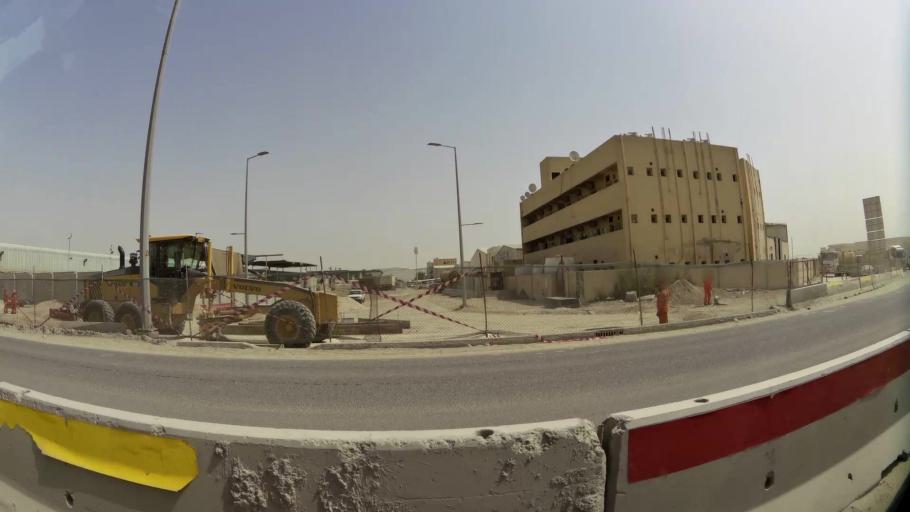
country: QA
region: Baladiyat ar Rayyan
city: Ar Rayyan
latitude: 25.1836
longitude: 51.4244
